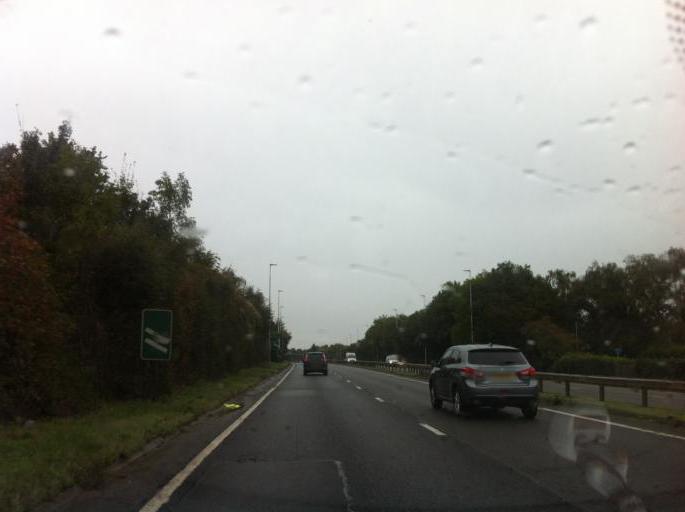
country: GB
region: England
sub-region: Peterborough
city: Peterborough
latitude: 52.5846
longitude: -0.2180
